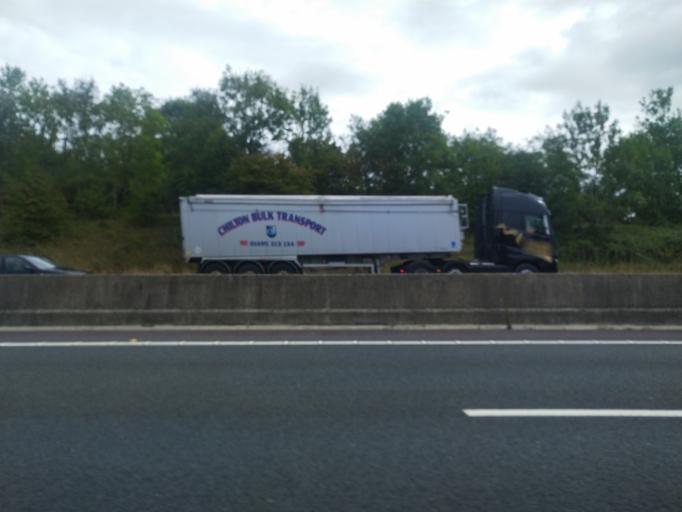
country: GB
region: England
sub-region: Wiltshire
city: Aldbourne
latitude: 51.4935
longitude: -1.5814
